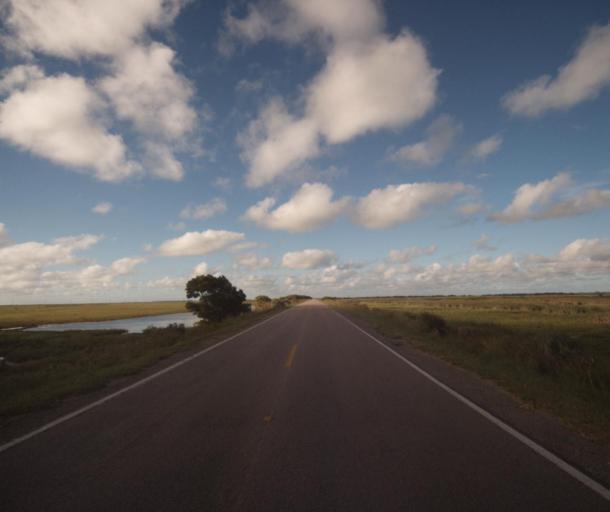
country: BR
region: Rio Grande do Sul
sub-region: Arroio Grande
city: Arroio Grande
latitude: -32.6054
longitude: -52.5712
